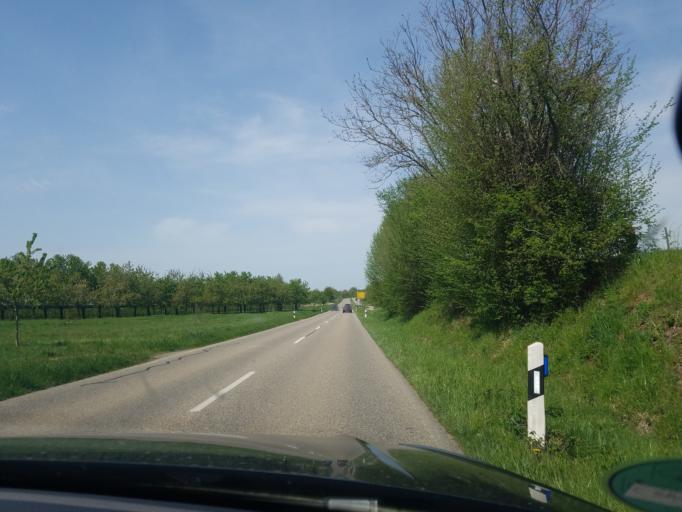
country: DE
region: Baden-Wuerttemberg
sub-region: Freiburg Region
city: Haslach
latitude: 48.5507
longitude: 8.0606
